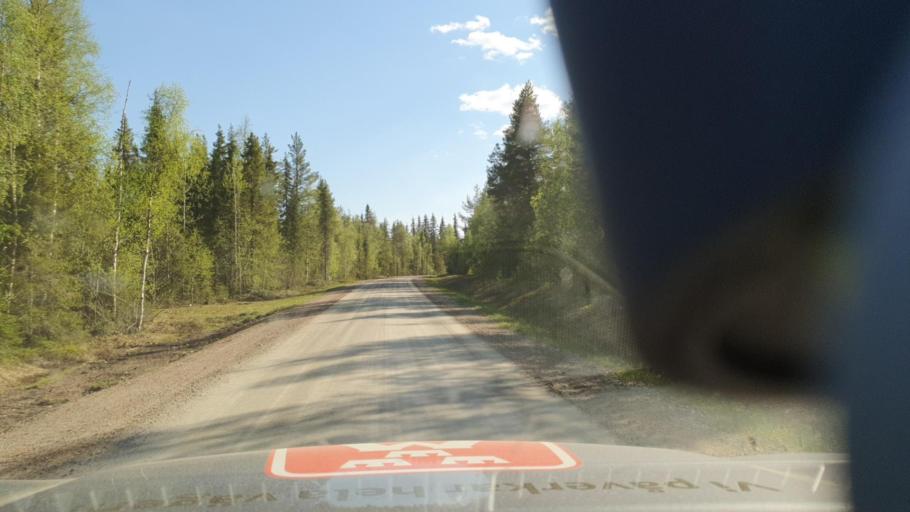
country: SE
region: Norrbotten
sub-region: Bodens Kommun
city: Boden
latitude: 66.3877
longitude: 21.6193
